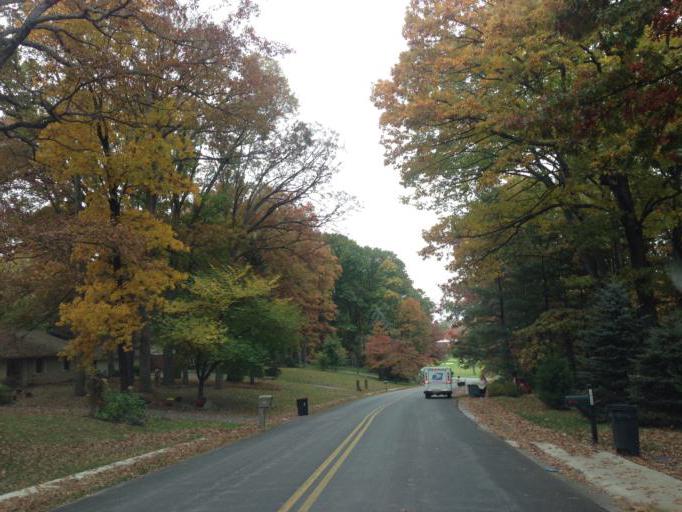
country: US
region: Maryland
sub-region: Howard County
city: Columbia
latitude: 39.2988
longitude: -76.8801
